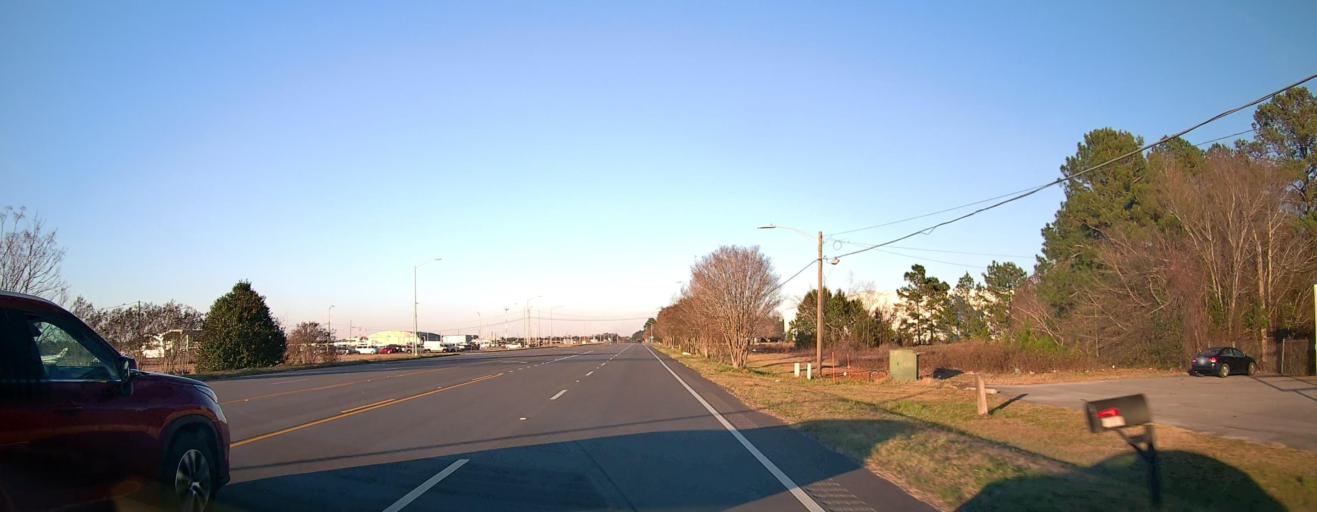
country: US
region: Georgia
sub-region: Dougherty County
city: Albany
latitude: 31.5294
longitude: -84.1892
